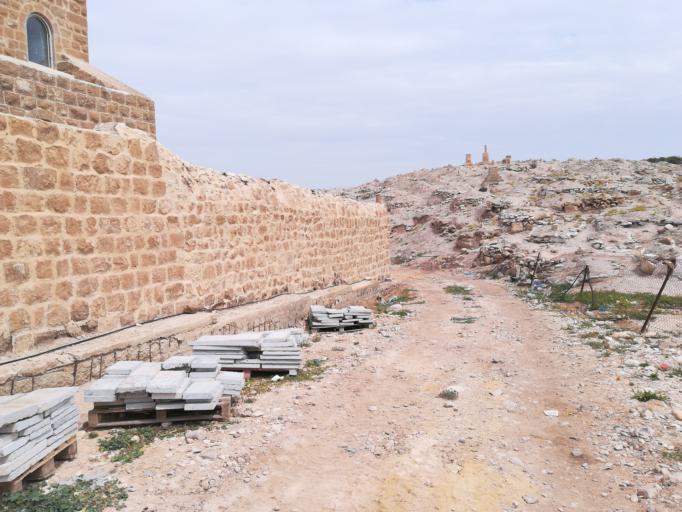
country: PS
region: West Bank
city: Jericho
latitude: 31.7861
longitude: 35.4318
